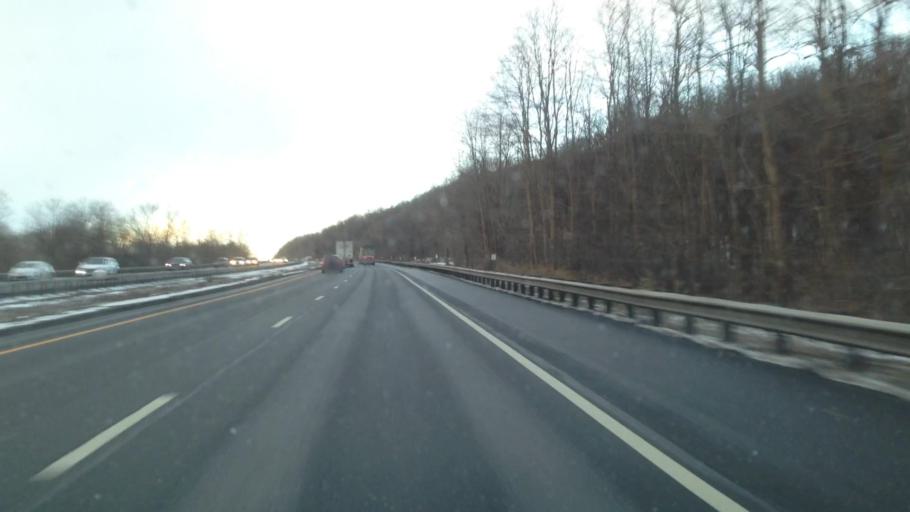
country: US
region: New York
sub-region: Herkimer County
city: Ilion
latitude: 43.0224
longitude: -75.0206
